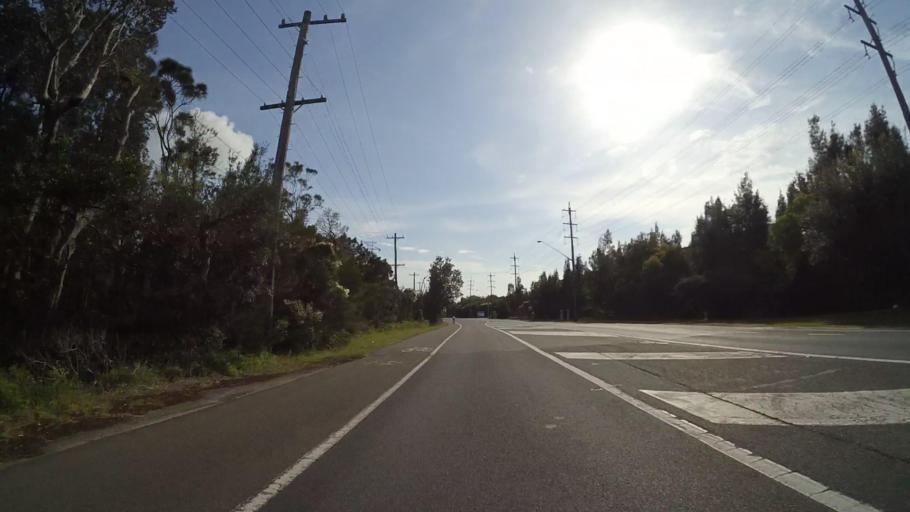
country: AU
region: New South Wales
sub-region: Sutherland Shire
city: Kurnell
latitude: -34.0193
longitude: 151.2029
